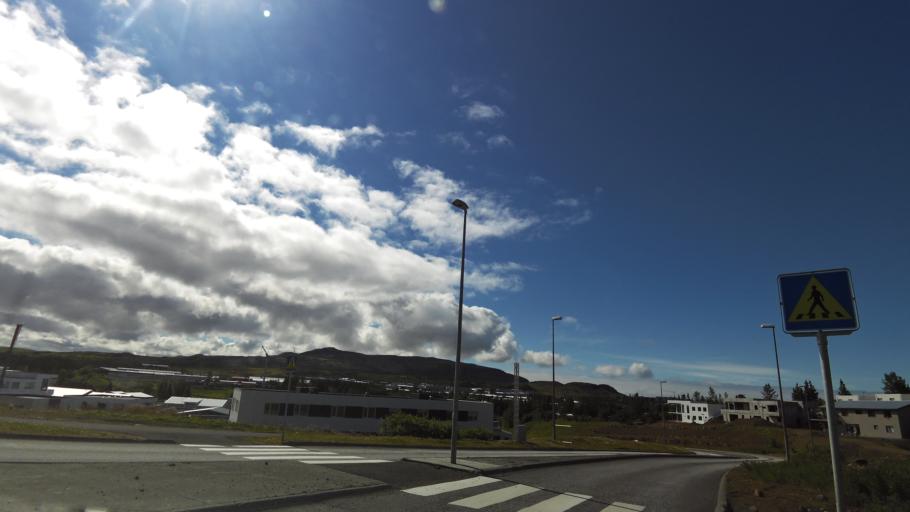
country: IS
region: Capital Region
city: Mosfellsbaer
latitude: 64.1692
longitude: -21.6720
